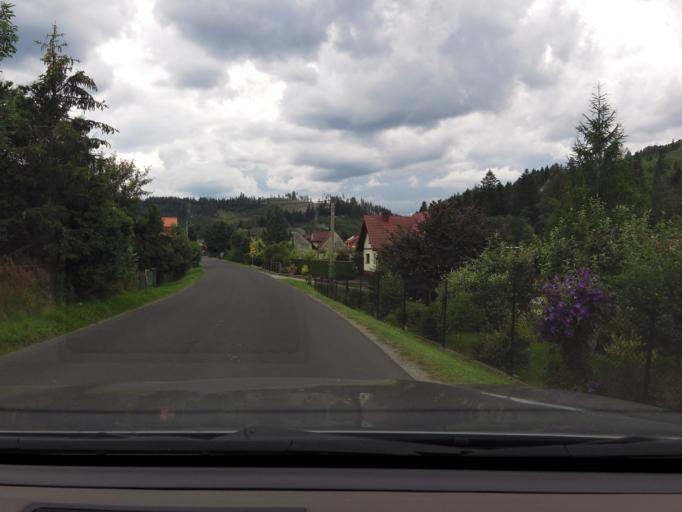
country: PL
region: Silesian Voivodeship
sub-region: Powiat zywiecki
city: Ujsoly
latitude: 49.4721
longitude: 19.1499
